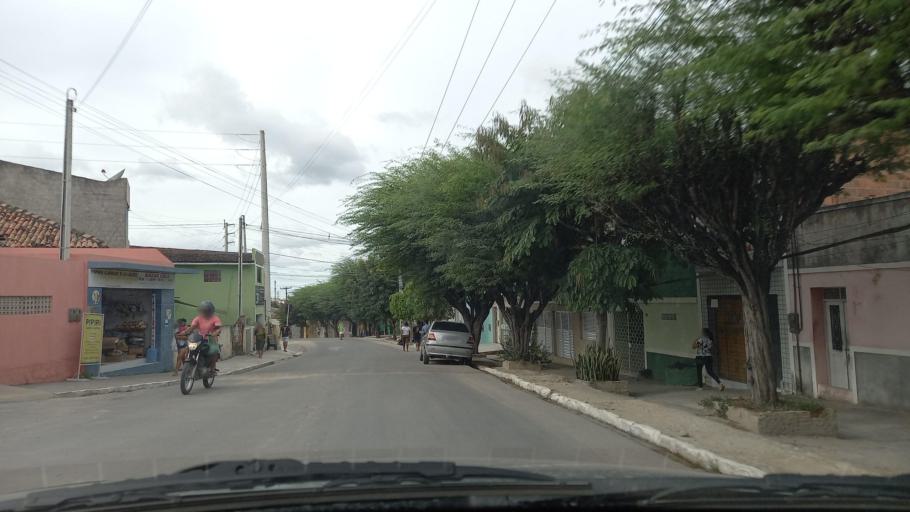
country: BR
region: Pernambuco
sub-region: Gravata
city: Gravata
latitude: -8.2078
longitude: -35.5699
